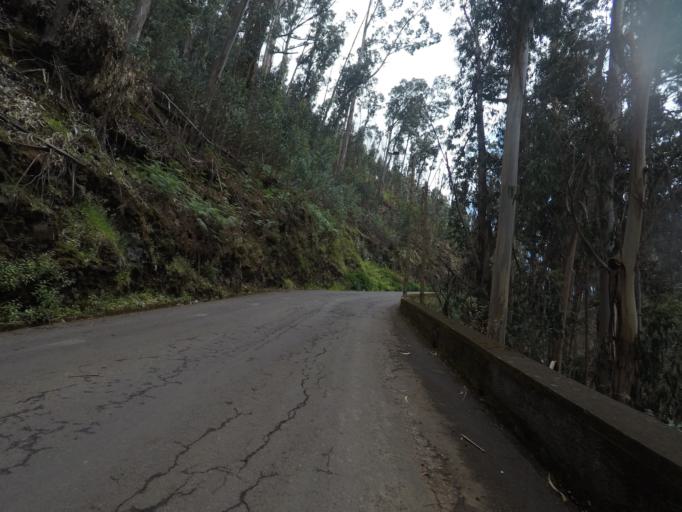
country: PT
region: Madeira
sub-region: Calheta
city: Estreito da Calheta
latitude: 32.7527
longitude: -17.1950
